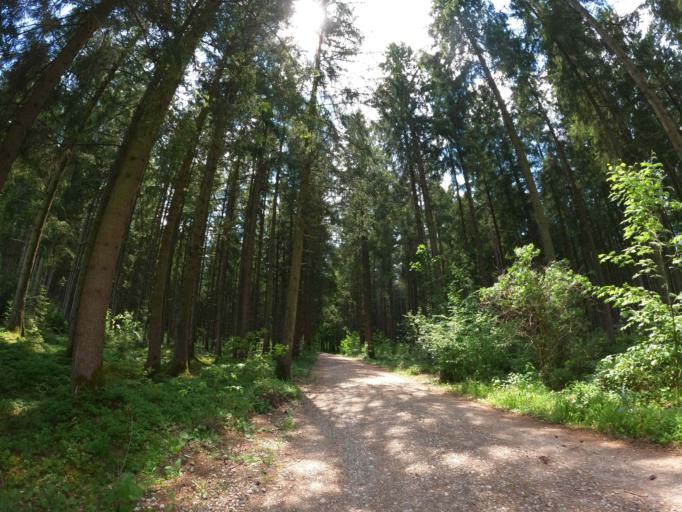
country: DE
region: Bavaria
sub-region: Upper Bavaria
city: Oberhaching
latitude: 48.0170
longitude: 11.6257
